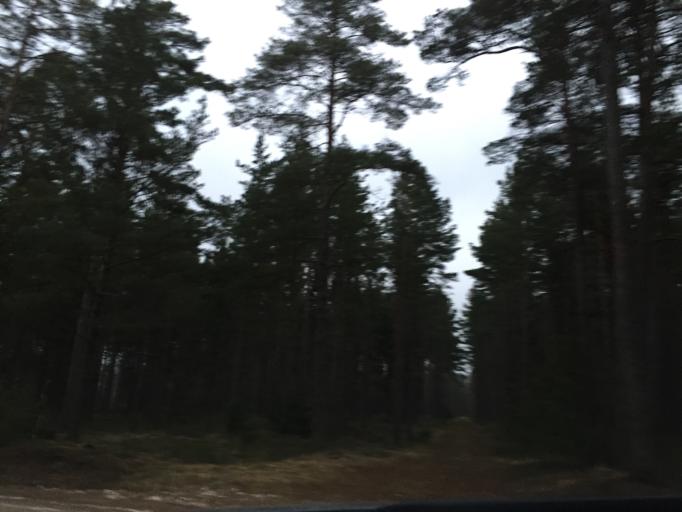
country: EE
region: Saare
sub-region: Kuressaare linn
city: Kuressaare
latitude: 58.5953
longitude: 22.5152
